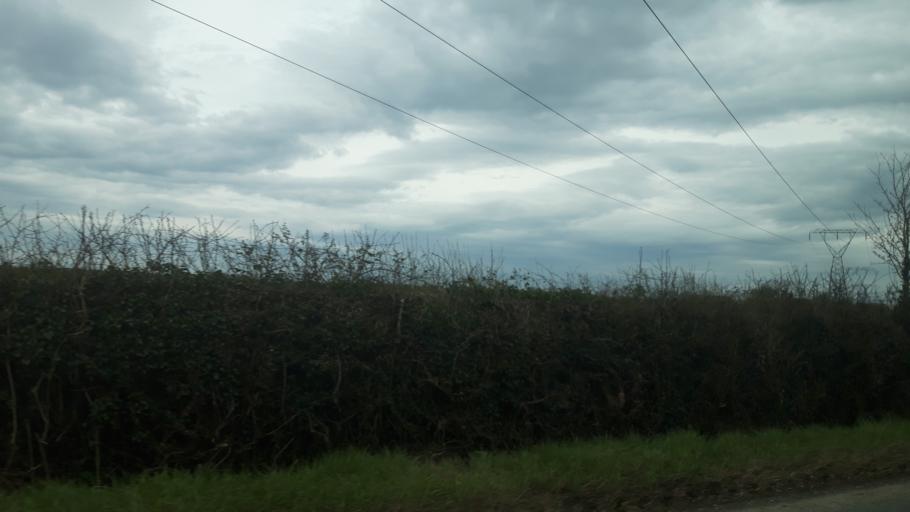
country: IE
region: Leinster
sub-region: Kildare
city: Prosperous
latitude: 53.3037
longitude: -6.7296
